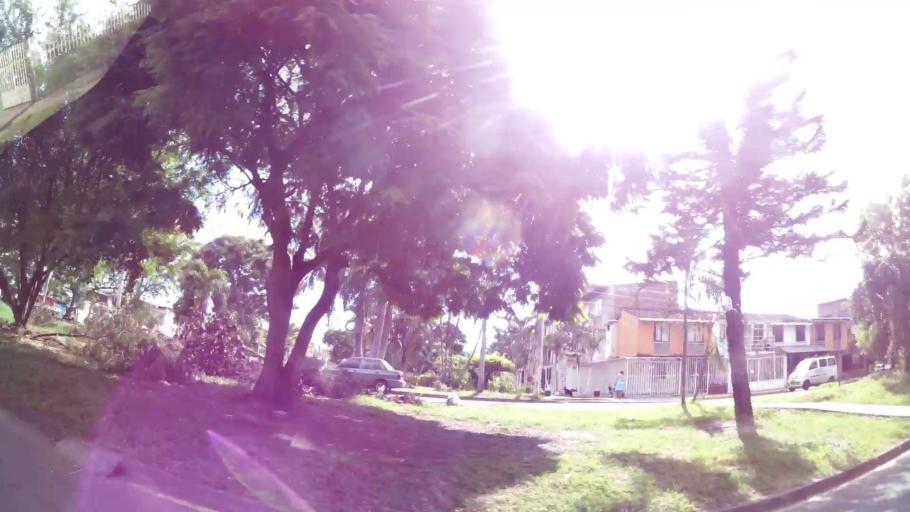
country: CO
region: Valle del Cauca
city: Cali
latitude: 3.3996
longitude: -76.5027
